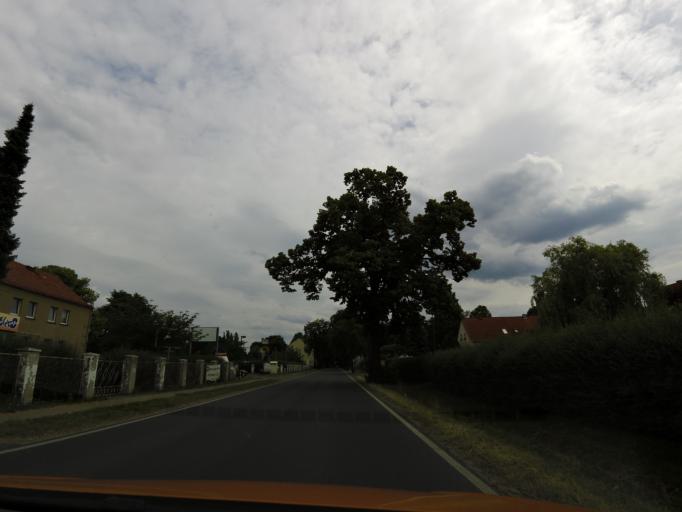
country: DE
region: Brandenburg
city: Zossen
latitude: 52.2226
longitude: 13.4282
